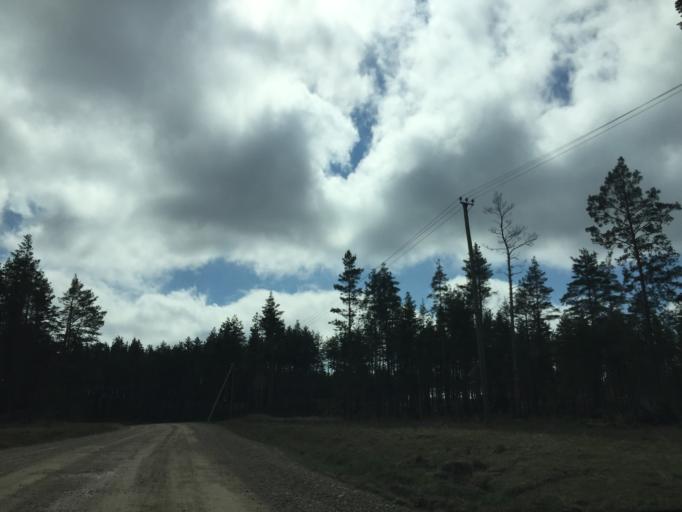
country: EE
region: Valgamaa
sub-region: Valga linn
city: Valga
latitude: 57.6488
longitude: 26.2213
